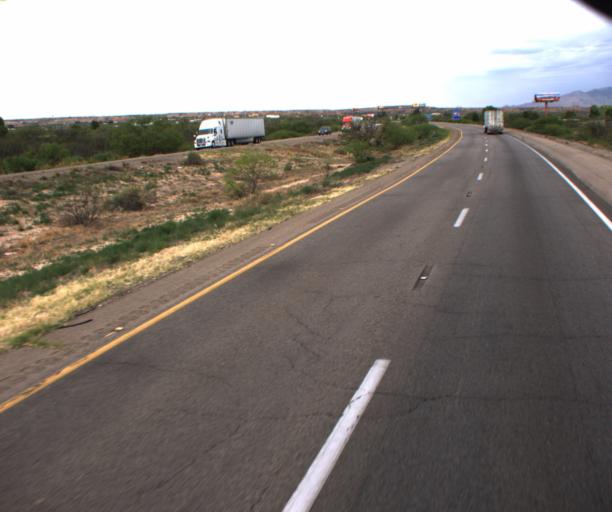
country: US
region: Arizona
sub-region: Cochise County
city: Benson
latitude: 31.9777
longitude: -110.2927
